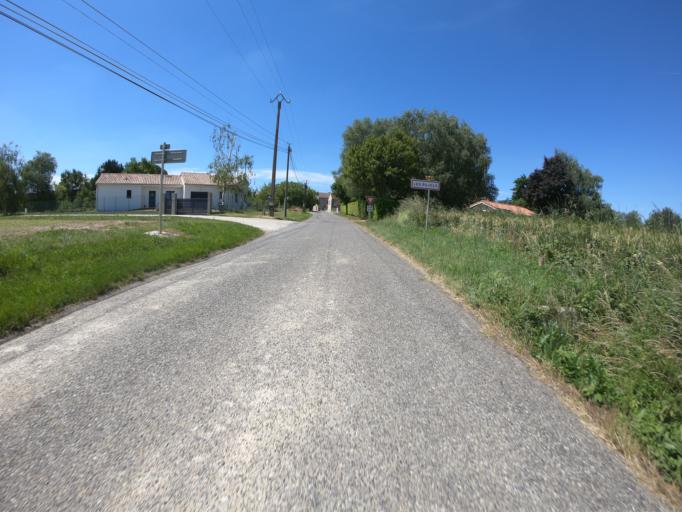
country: FR
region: Midi-Pyrenees
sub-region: Departement de l'Ariege
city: La Tour-du-Crieu
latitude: 43.0944
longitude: 1.7261
